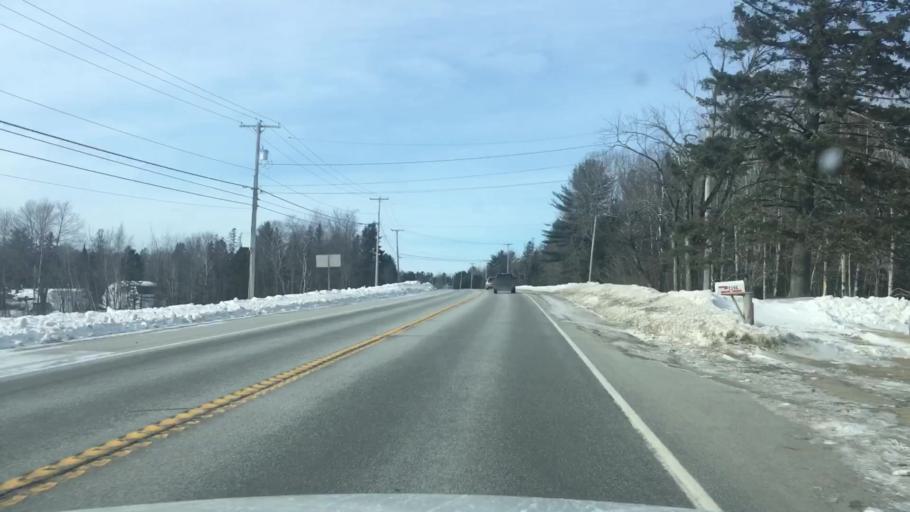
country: US
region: Maine
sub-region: Penobscot County
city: Kenduskeag
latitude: 44.9534
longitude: -68.9496
